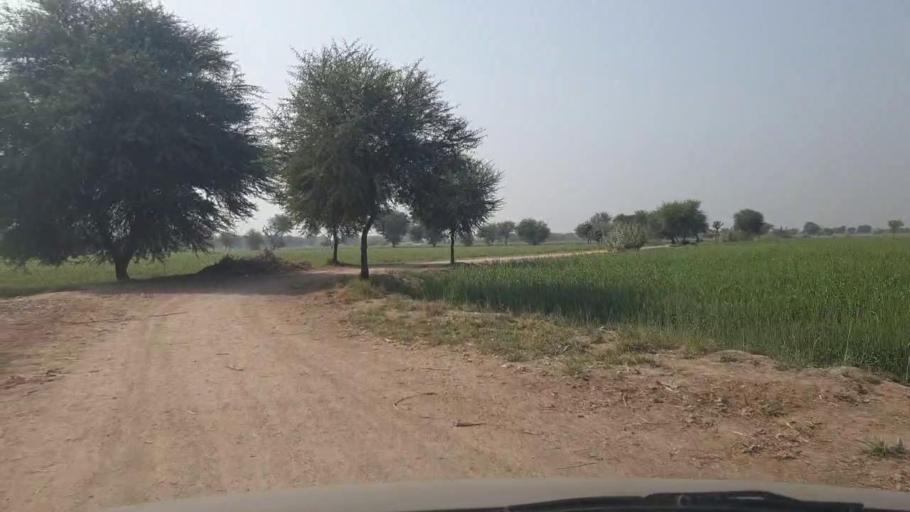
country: PK
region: Sindh
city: Umarkot
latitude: 25.4040
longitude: 69.7129
